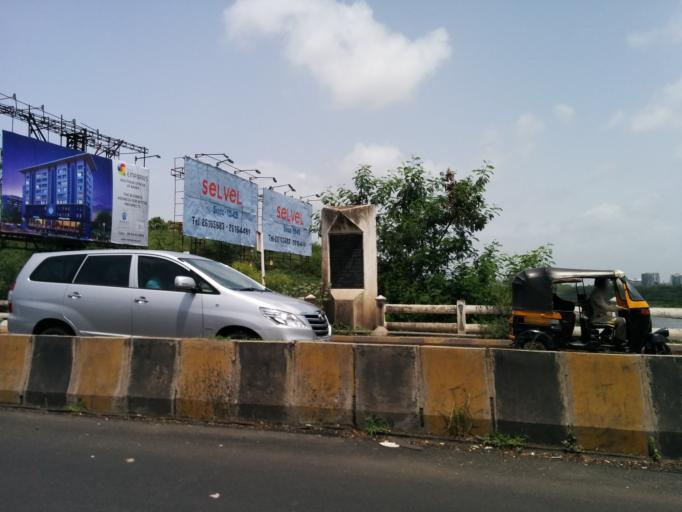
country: IN
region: Maharashtra
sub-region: Pune Division
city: Shivaji Nagar
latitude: 18.5402
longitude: 73.9040
